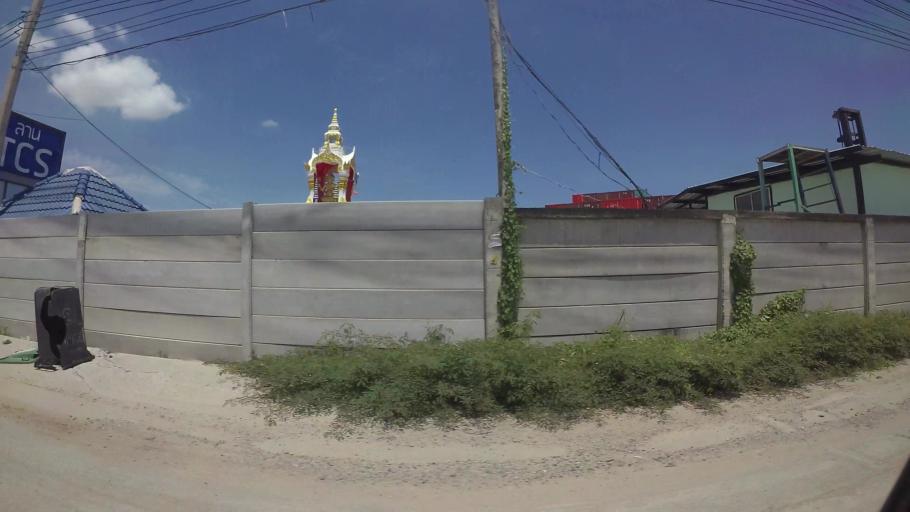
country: TH
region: Chon Buri
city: Si Racha
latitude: 13.1214
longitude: 100.9553
